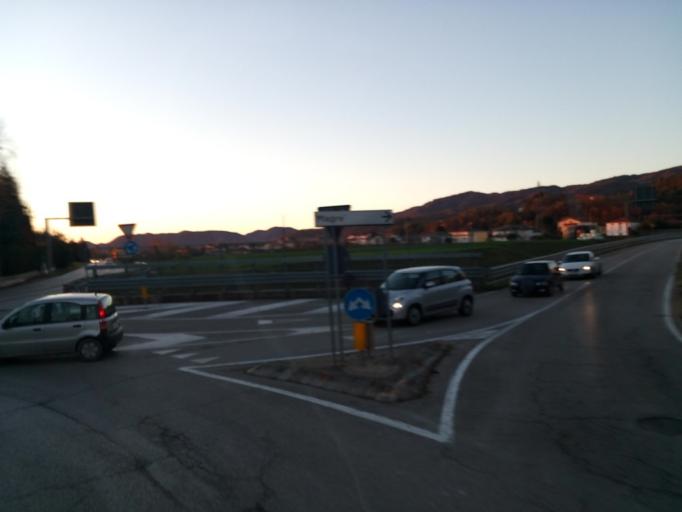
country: IT
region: Veneto
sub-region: Provincia di Vicenza
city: Schio
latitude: 45.7016
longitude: 11.3653
